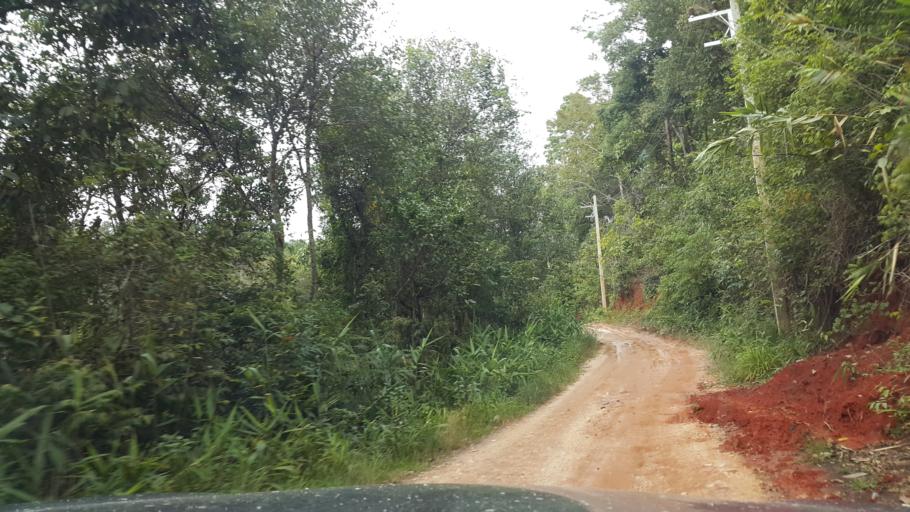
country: TH
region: Chiang Mai
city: Samoeng
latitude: 18.8792
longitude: 98.5103
